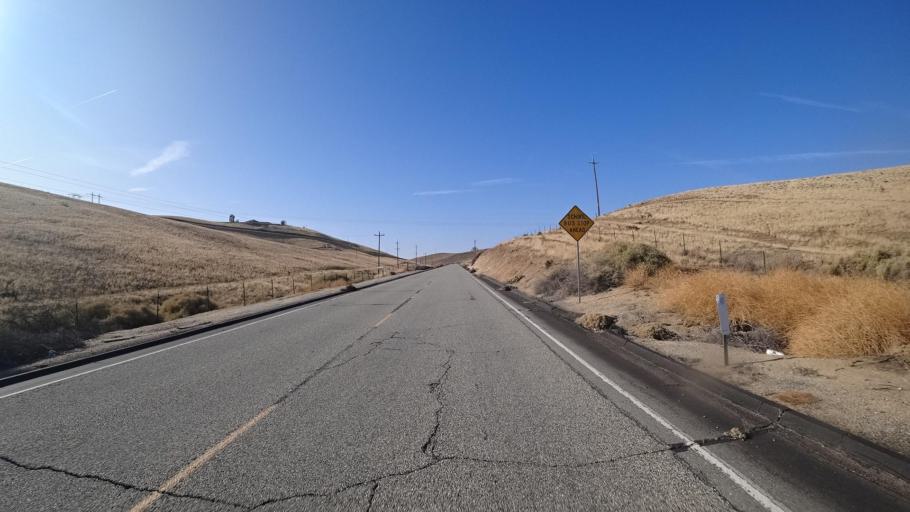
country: US
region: California
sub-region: Kern County
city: Oildale
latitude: 35.5024
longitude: -118.9898
